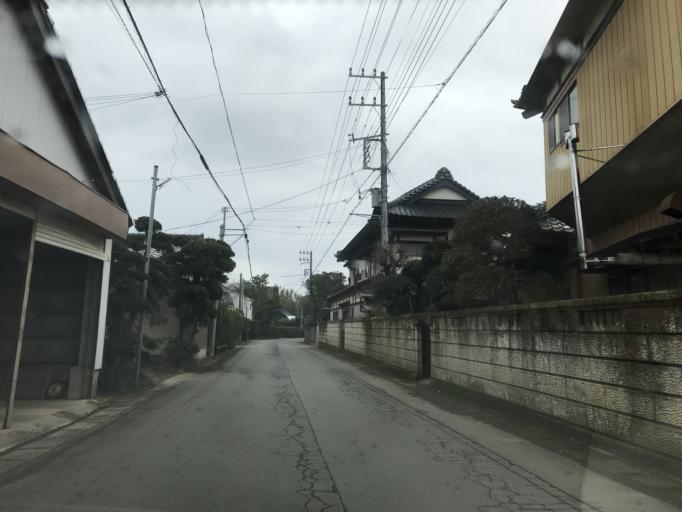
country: JP
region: Chiba
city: Sawara
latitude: 35.8515
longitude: 140.5436
